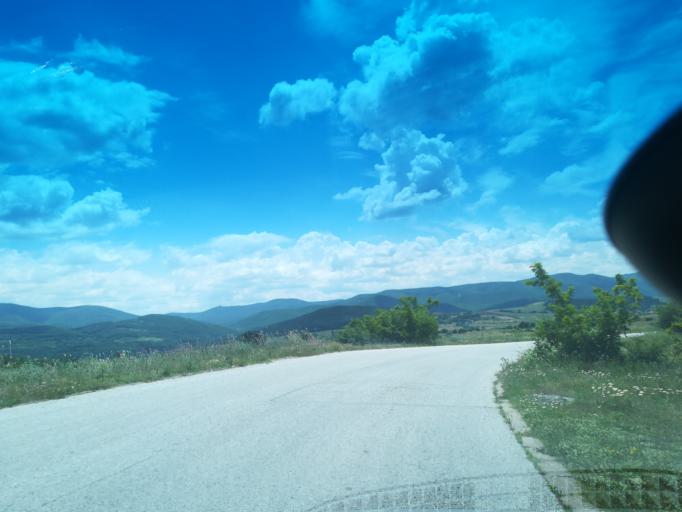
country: BG
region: Khaskovo
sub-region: Obshtina Mineralni Bani
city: Mineralni Bani
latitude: 41.9571
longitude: 25.2625
